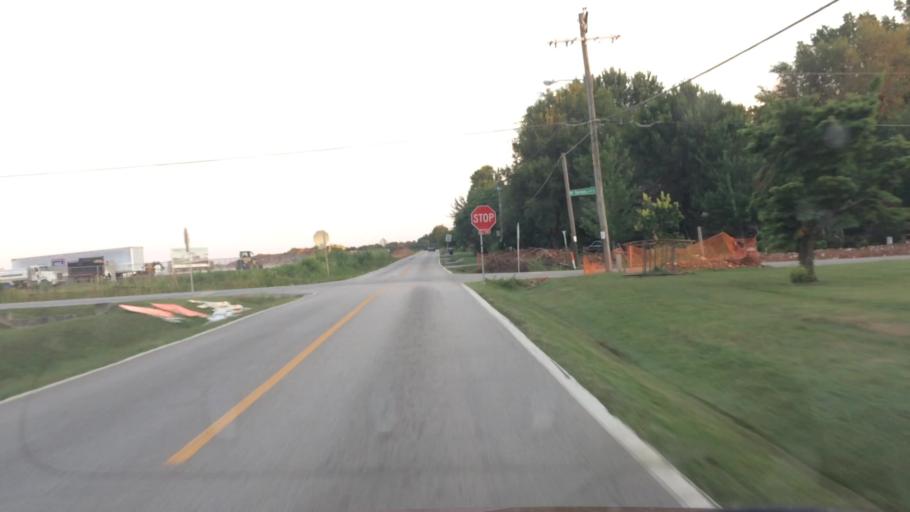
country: US
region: Missouri
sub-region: Greene County
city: Springfield
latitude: 37.2055
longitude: -93.3742
